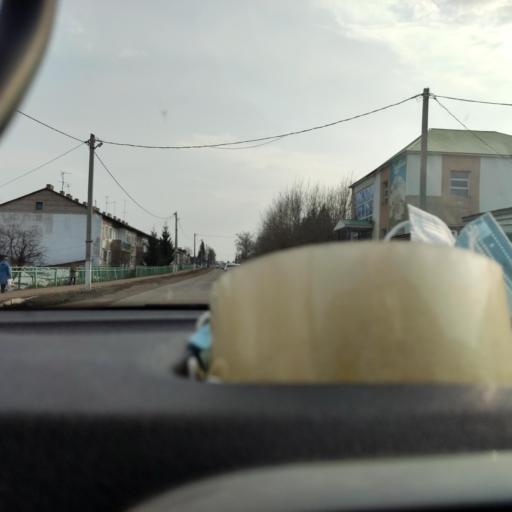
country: RU
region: Bashkortostan
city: Ulukulevo
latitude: 54.3760
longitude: 56.4497
